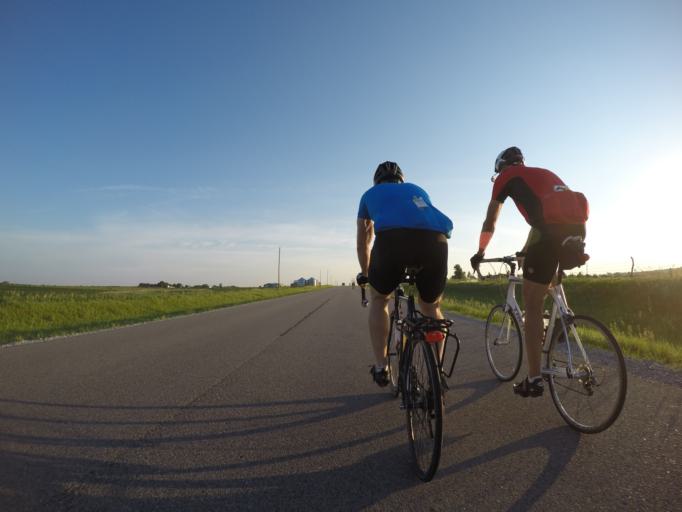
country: US
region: Kansas
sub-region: Marshall County
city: Marysville
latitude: 39.8518
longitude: -96.6009
